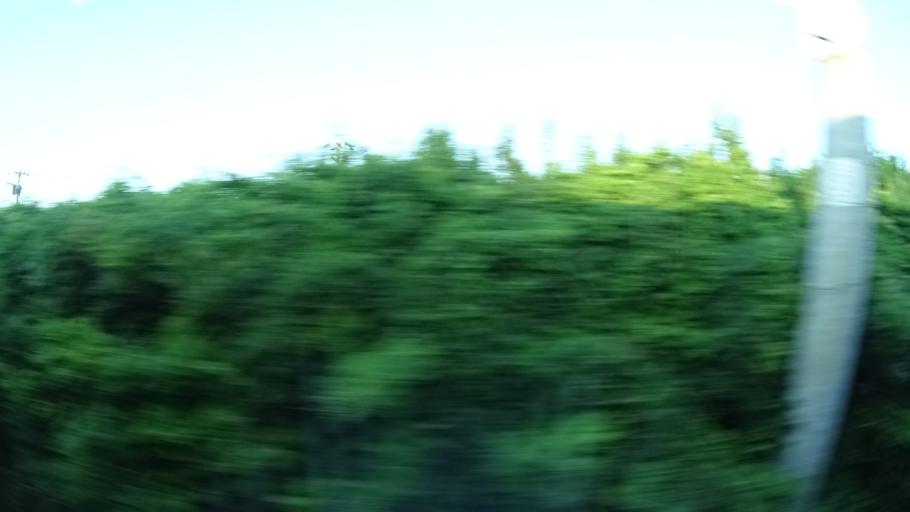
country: JP
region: Ibaraki
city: Ishioka
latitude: 36.2526
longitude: 140.2856
